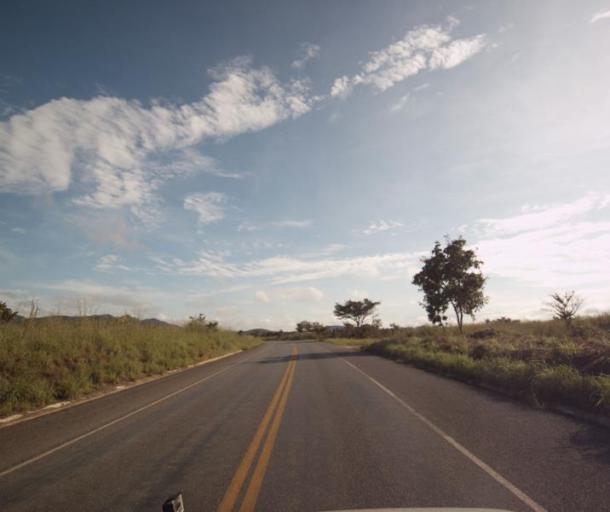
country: BR
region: Goias
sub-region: Pirenopolis
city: Pirenopolis
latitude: -15.5685
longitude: -48.6216
